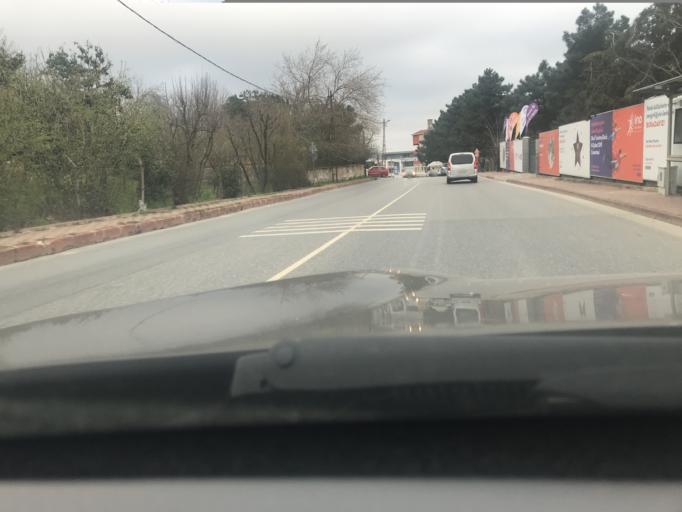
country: TR
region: Istanbul
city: Umraniye
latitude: 41.0522
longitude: 29.1717
